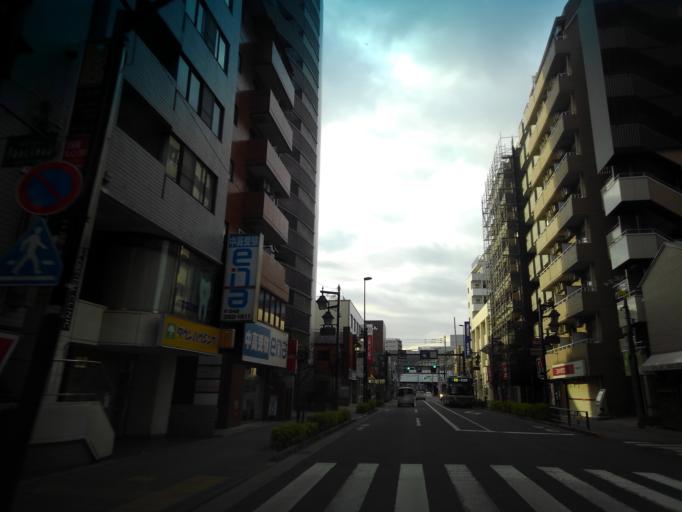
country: JP
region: Tokyo
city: Kokubunji
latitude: 35.7029
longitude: 139.5074
